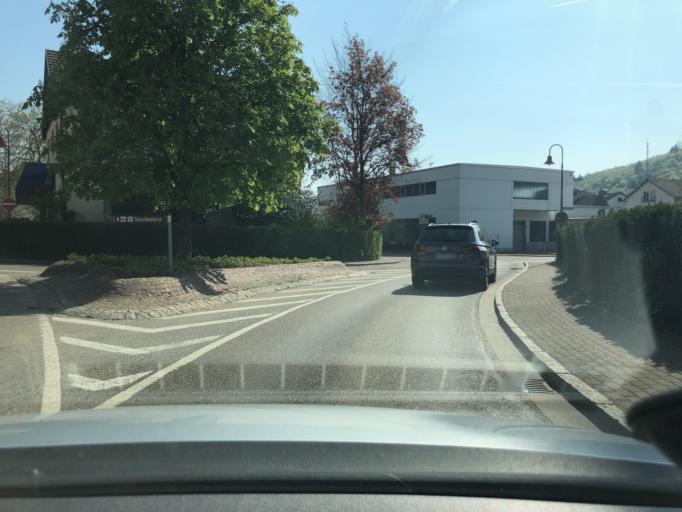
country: DE
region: Baden-Wuerttemberg
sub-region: Freiburg Region
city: Lauchringen
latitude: 47.6342
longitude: 8.2760
